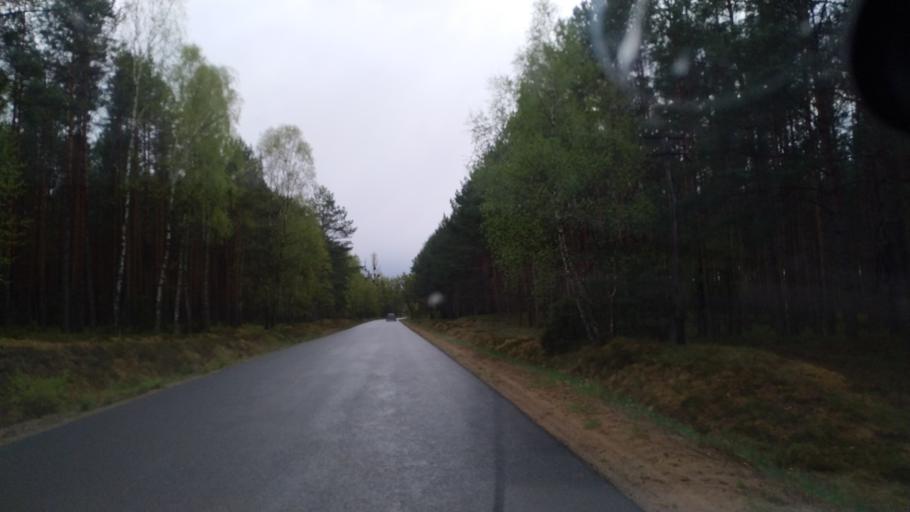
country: PL
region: Pomeranian Voivodeship
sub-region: Powiat starogardzki
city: Osiek
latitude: 53.6471
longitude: 18.4896
